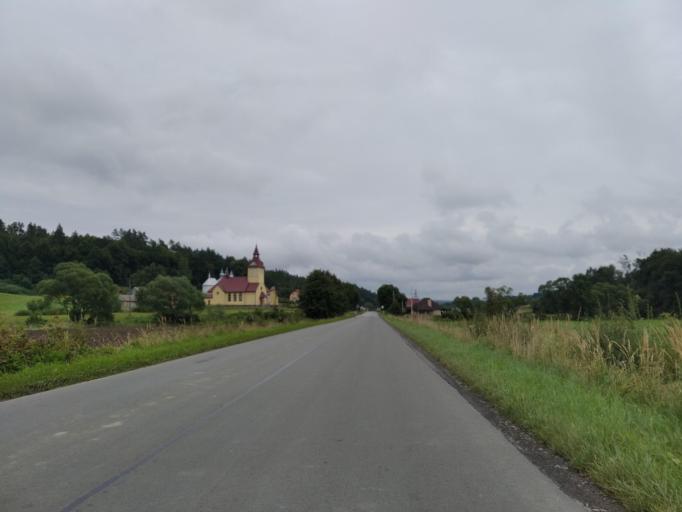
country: PL
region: Subcarpathian Voivodeship
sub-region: Powiat przemyski
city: Bircza
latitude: 49.7000
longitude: 22.3746
